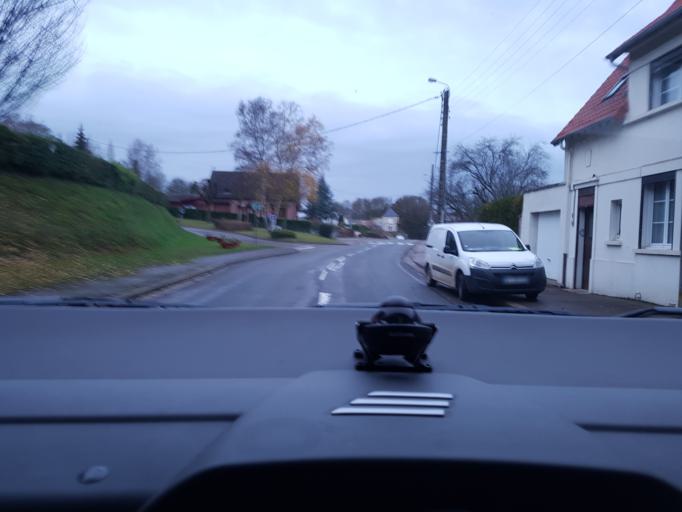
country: FR
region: Picardie
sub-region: Departement de la Somme
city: Poix-de-Picardie
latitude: 49.7746
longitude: 1.9794
